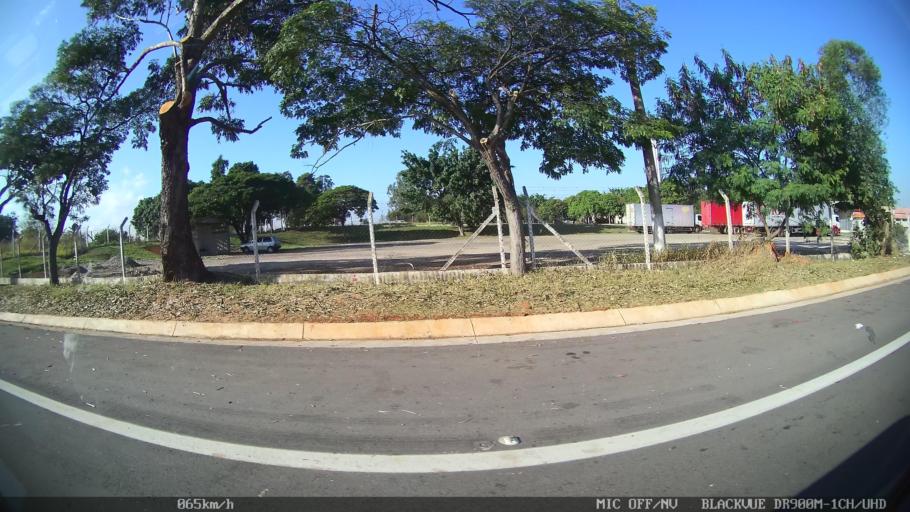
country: BR
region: Sao Paulo
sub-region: Hortolandia
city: Hortolandia
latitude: -22.8861
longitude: -47.1586
